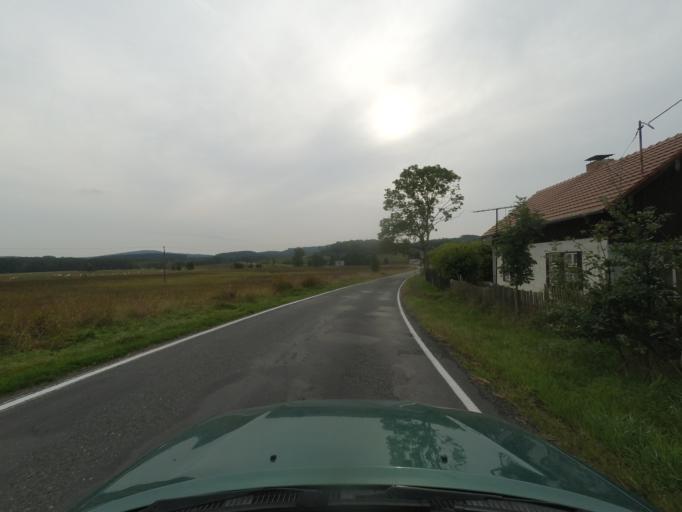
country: DE
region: Bavaria
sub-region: Upper Palatinate
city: Eslarn
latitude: 49.5876
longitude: 12.5948
